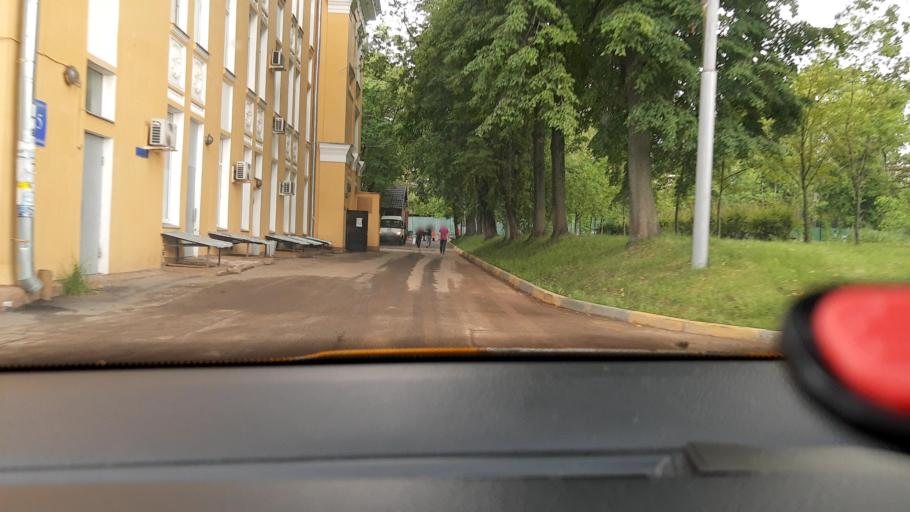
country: RU
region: Moscow
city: Lefortovo
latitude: 55.7694
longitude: 37.7389
